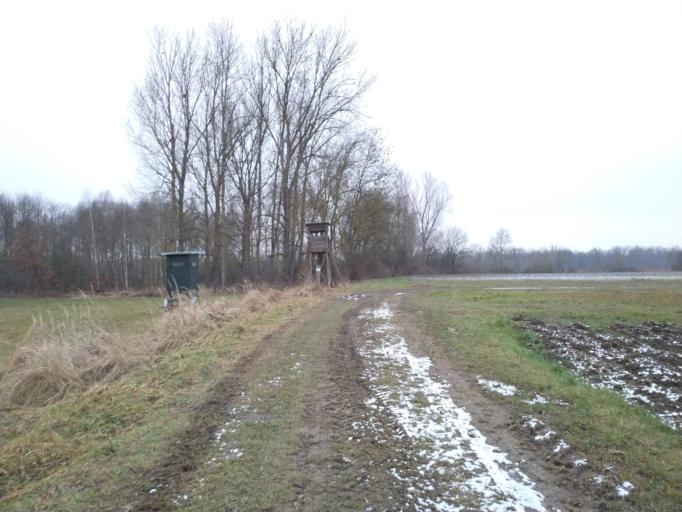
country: DE
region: Bavaria
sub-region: Swabia
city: Offingen
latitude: 48.4912
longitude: 10.3475
